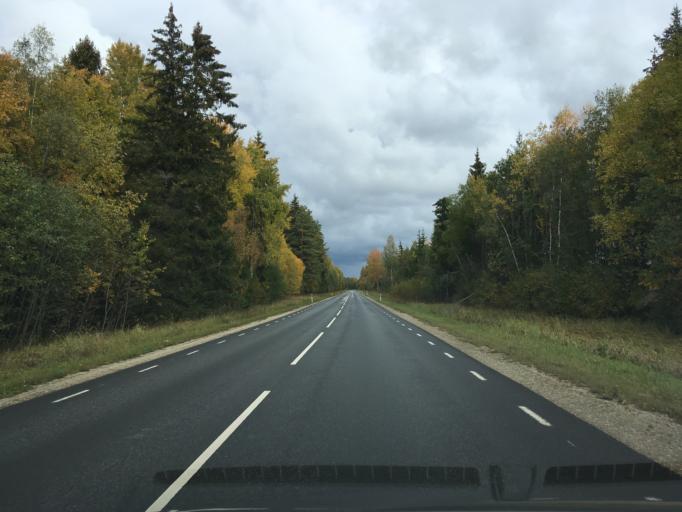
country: EE
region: Harju
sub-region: Anija vald
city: Kehra
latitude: 59.2641
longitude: 25.3529
